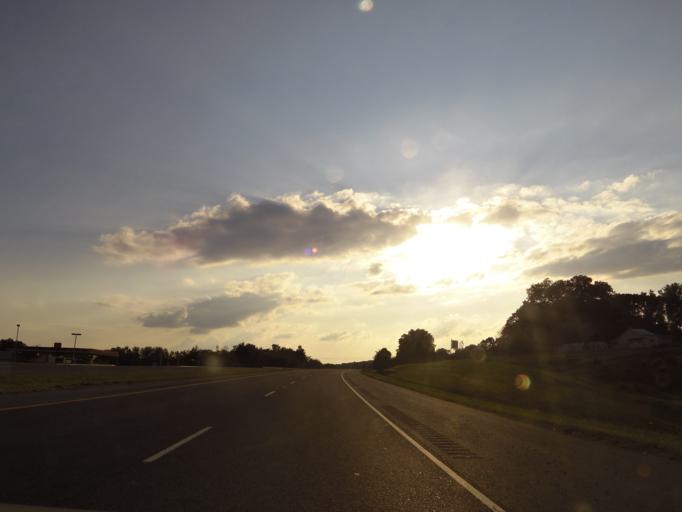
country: US
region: Tennessee
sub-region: Knox County
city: Mascot
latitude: 36.0476
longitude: -83.8074
